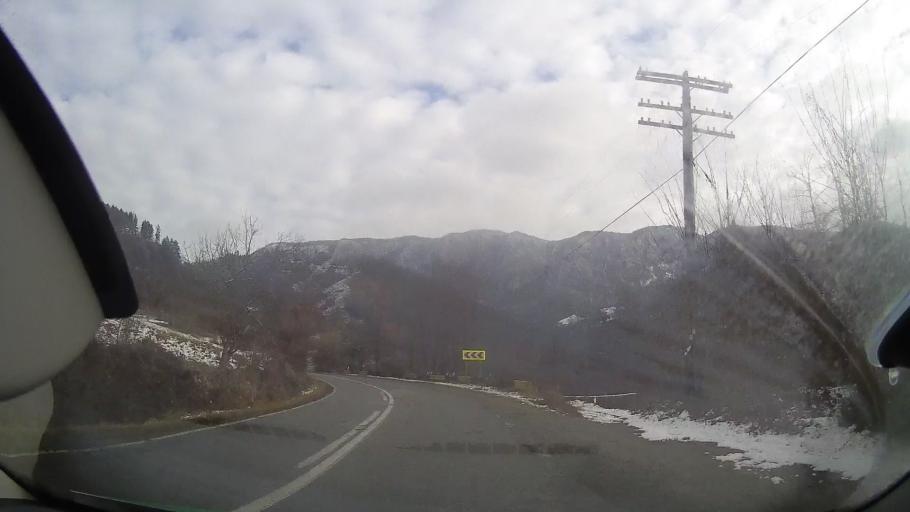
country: RO
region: Alba
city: Salciua de Sus
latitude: 46.4064
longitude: 23.4446
